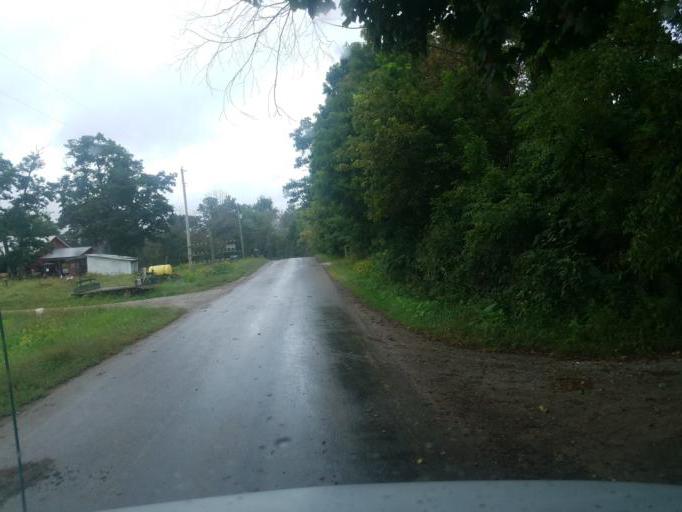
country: US
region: Ohio
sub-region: Wayne County
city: West Salem
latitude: 40.9465
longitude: -82.1190
